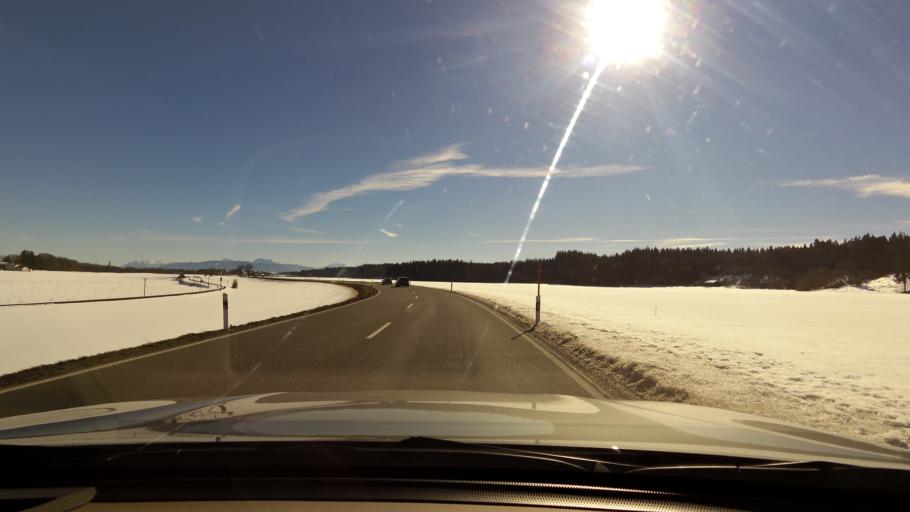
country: DE
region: Bavaria
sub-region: Upper Bavaria
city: Traunreut
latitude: 47.9555
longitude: 12.5681
